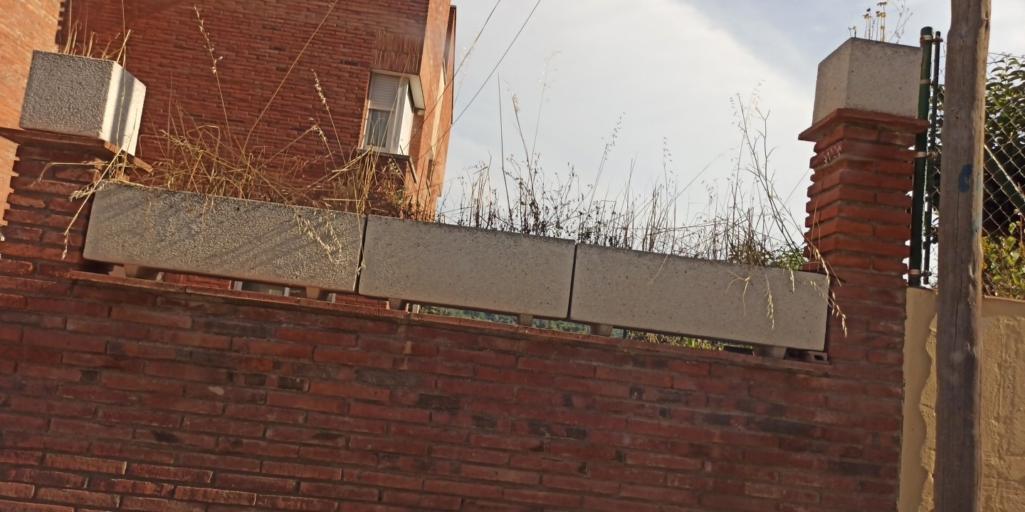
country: ES
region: Catalonia
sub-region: Provincia de Barcelona
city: Santa Coloma de Cervello
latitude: 41.3499
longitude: 2.0138
